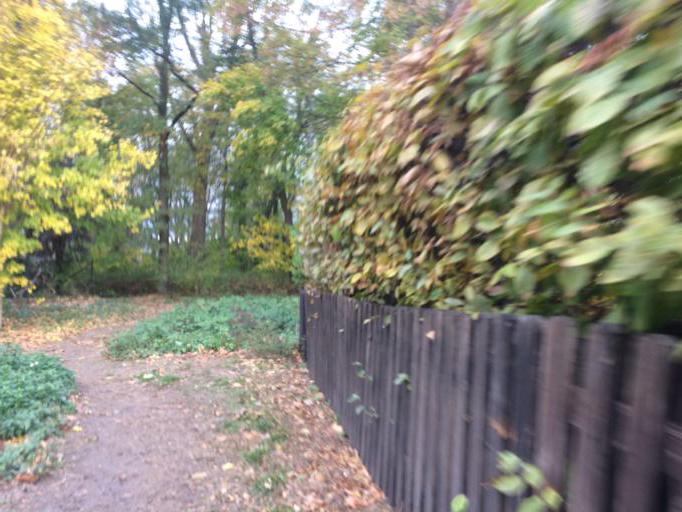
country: DE
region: Berlin
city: Wittenau
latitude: 52.5917
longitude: 13.3188
